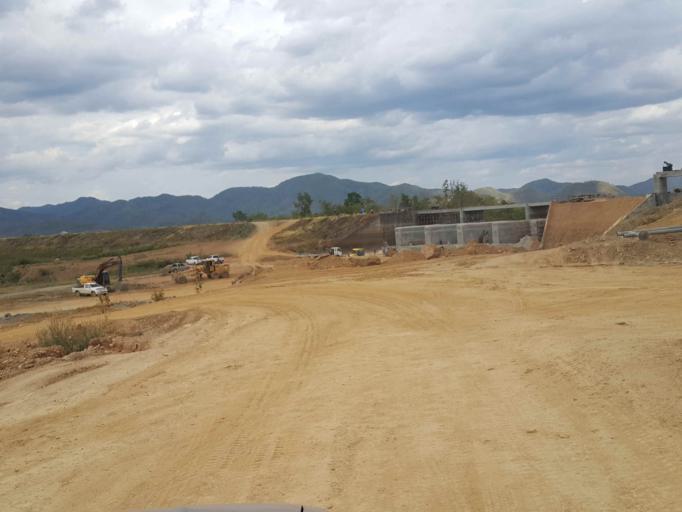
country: TH
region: Sukhothai
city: Thung Saliam
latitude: 17.3099
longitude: 99.4246
